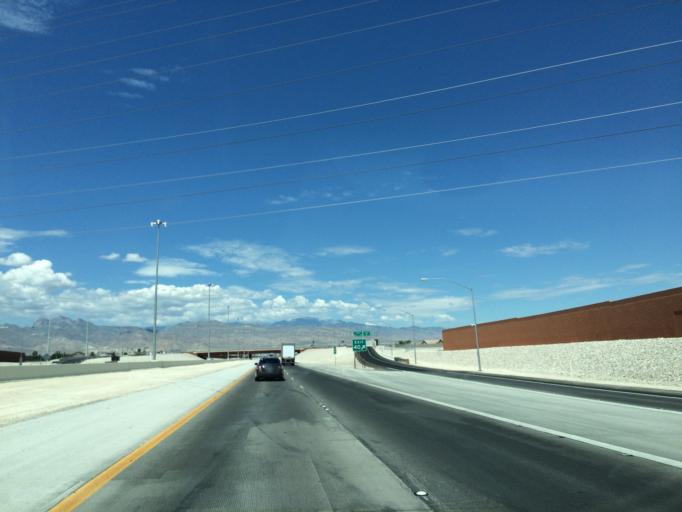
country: US
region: Nevada
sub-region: Clark County
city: North Las Vegas
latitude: 36.2753
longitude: -115.2187
